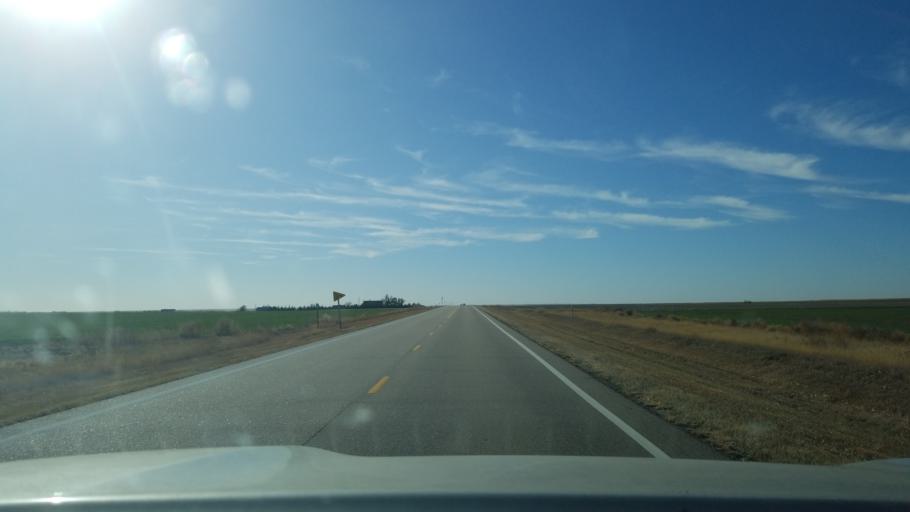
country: US
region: Kansas
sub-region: Ness County
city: Ness City
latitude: 38.3382
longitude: -99.8977
